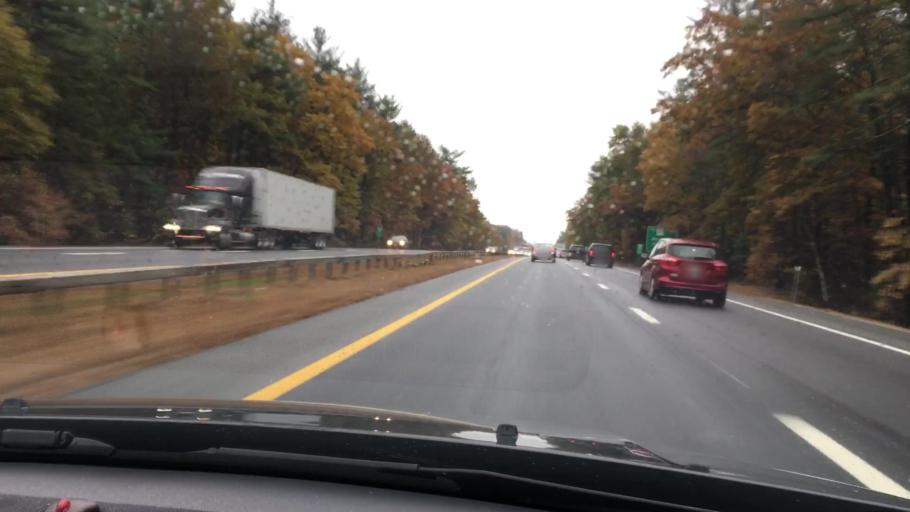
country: US
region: New Hampshire
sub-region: Hillsborough County
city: Nashua
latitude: 42.8005
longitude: -71.4981
